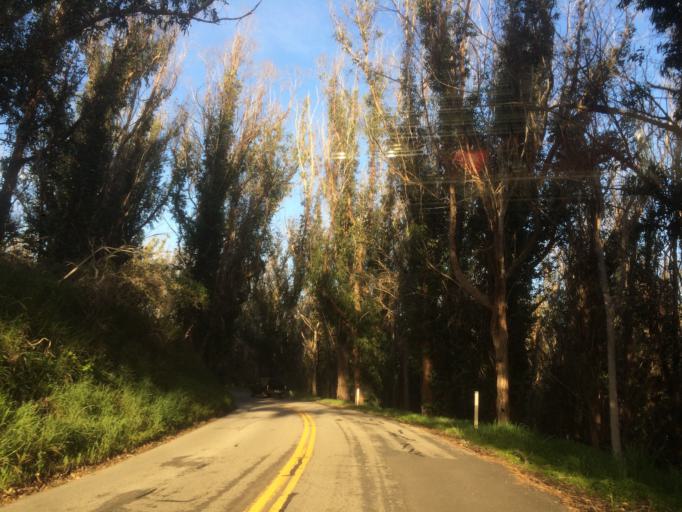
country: US
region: California
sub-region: San Luis Obispo County
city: Los Osos
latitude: 35.2947
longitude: -120.8709
